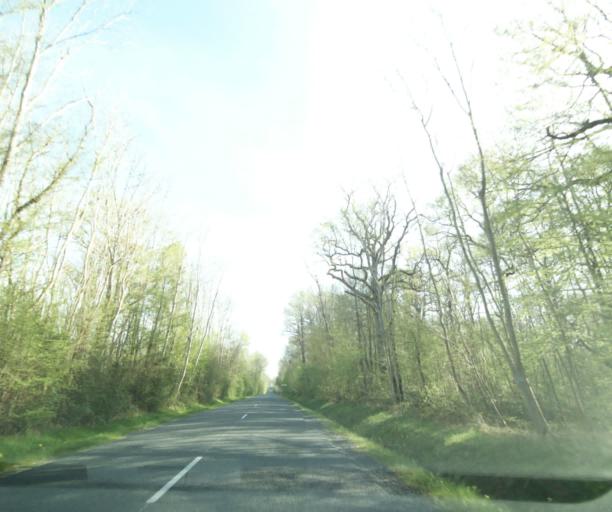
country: FR
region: Ile-de-France
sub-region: Departement de Seine-et-Marne
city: Nangis
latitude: 48.5271
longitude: 2.9768
